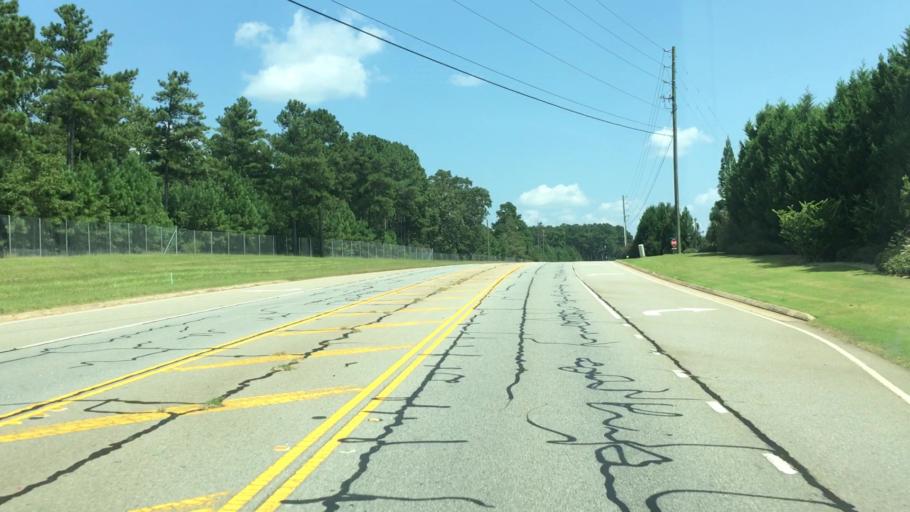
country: US
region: Georgia
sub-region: Oconee County
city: Watkinsville
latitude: 33.8684
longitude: -83.4737
